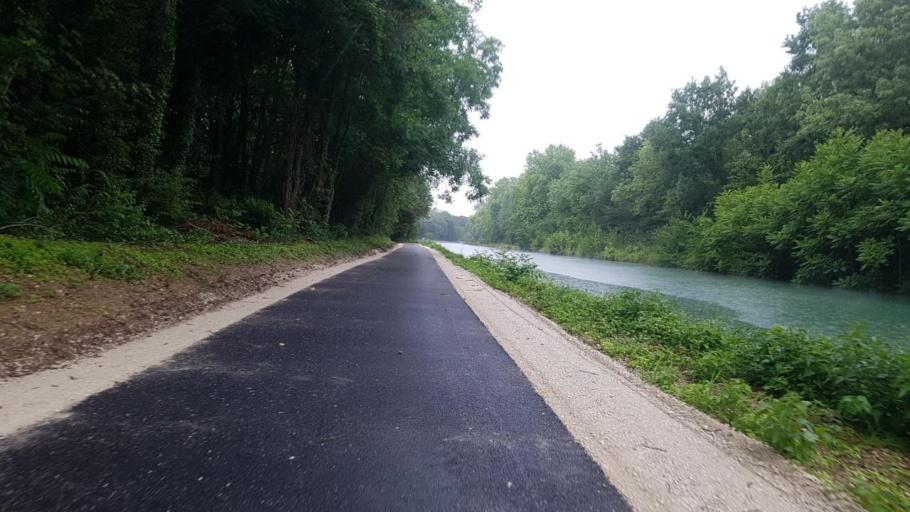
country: FR
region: Champagne-Ardenne
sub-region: Departement de la Marne
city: Sarry
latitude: 48.8680
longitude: 4.4616
